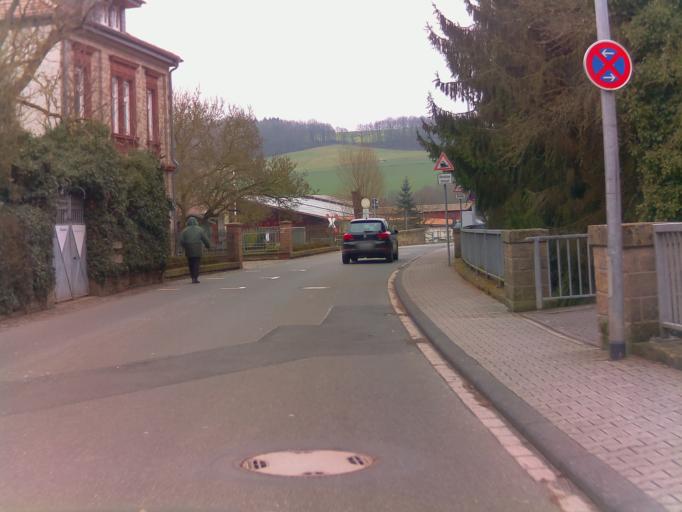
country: DE
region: Rheinland-Pfalz
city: Raumbach
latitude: 49.7240
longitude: 7.6626
